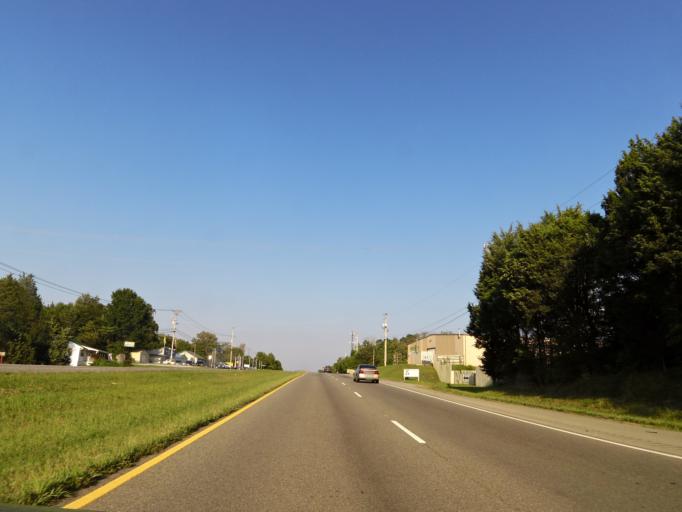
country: US
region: Tennessee
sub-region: Knox County
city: Mascot
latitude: 36.0245
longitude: -83.7451
